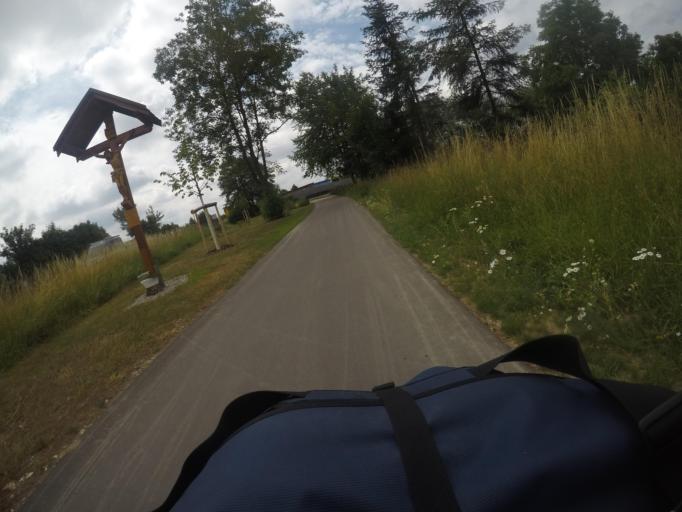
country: DE
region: Bavaria
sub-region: Swabia
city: Vohringen
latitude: 48.2904
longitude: 10.0763
